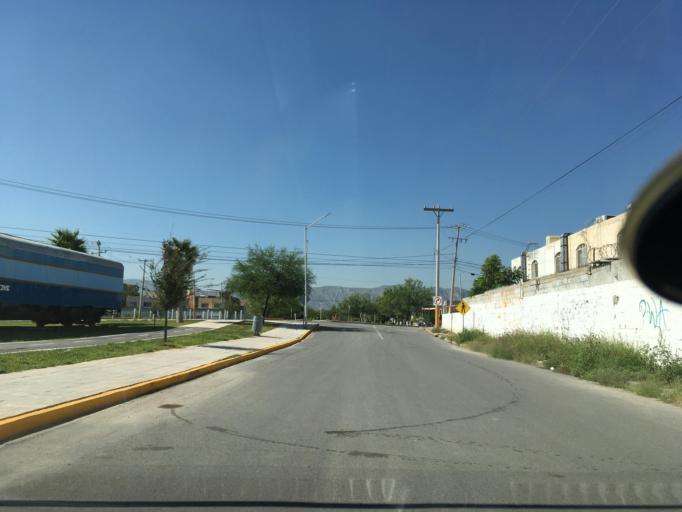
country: MX
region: Coahuila
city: Torreon
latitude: 25.5225
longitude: -103.3791
